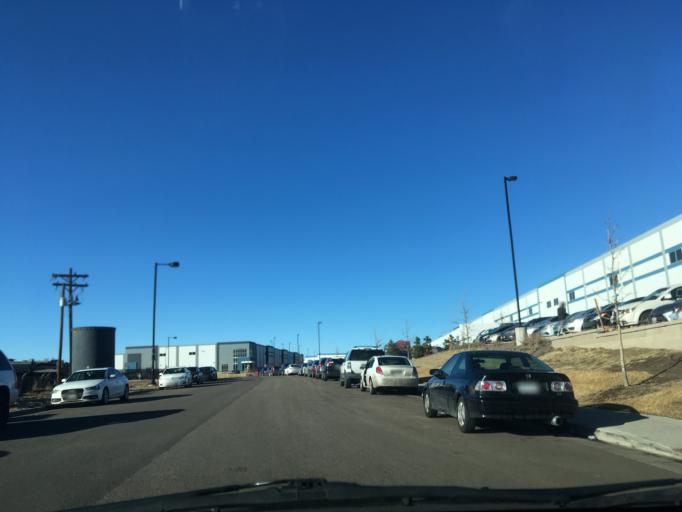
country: US
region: Colorado
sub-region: Adams County
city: Twin Lakes
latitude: 39.7926
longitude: -104.9819
